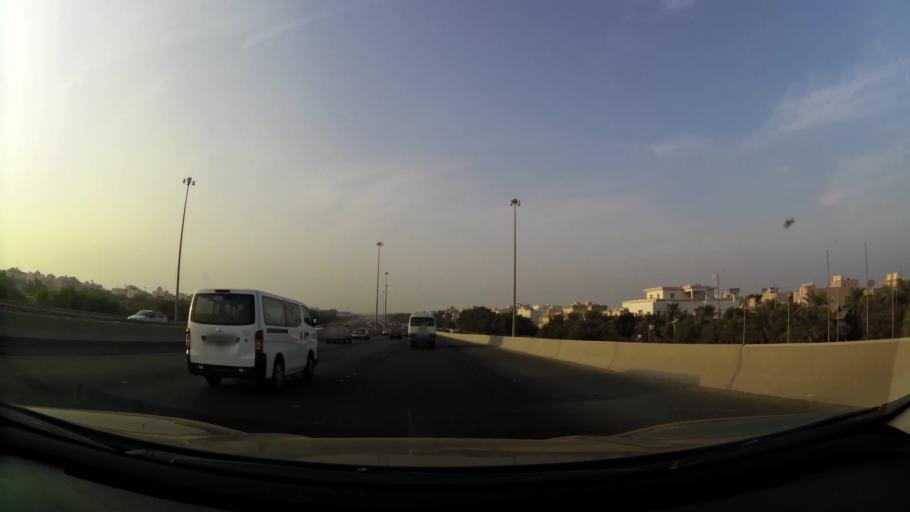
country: KW
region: Muhafazat Hawalli
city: Salwa
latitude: 29.2708
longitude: 48.0845
